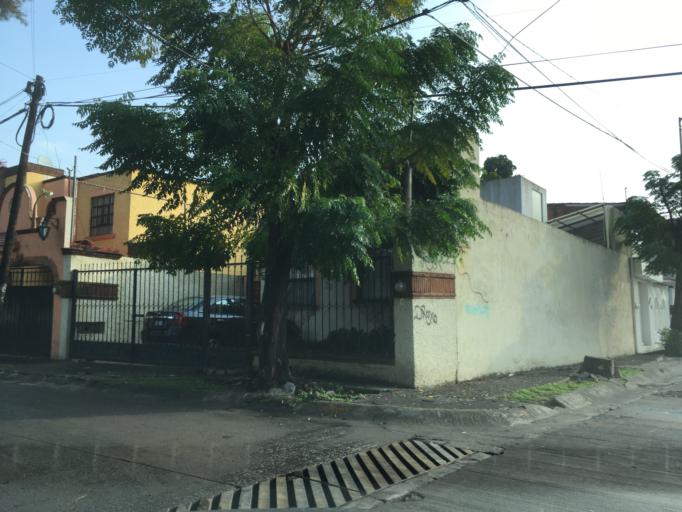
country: MX
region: Michoacan
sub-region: Morelia
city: Morelos
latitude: 19.6808
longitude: -101.2235
